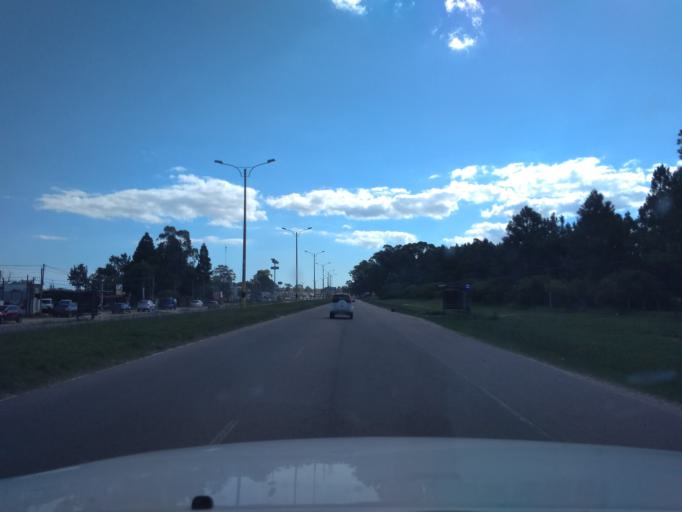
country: UY
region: Canelones
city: Barra de Carrasco
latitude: -34.8453
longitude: -56.0012
